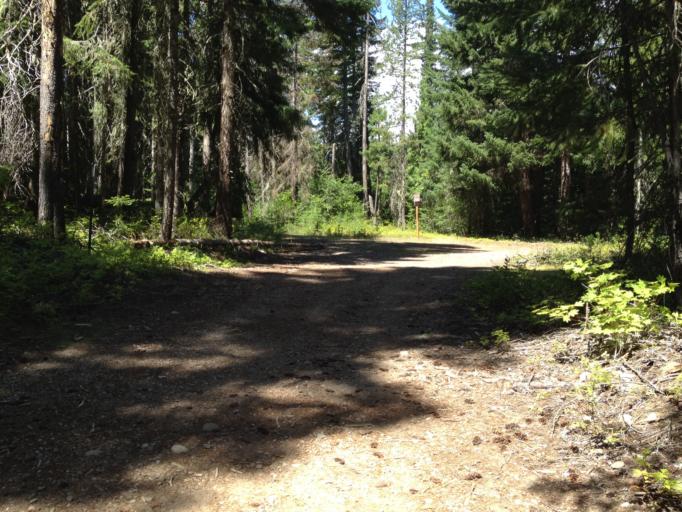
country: US
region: Washington
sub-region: Kittitas County
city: Cle Elum
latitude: 47.2551
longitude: -121.2086
